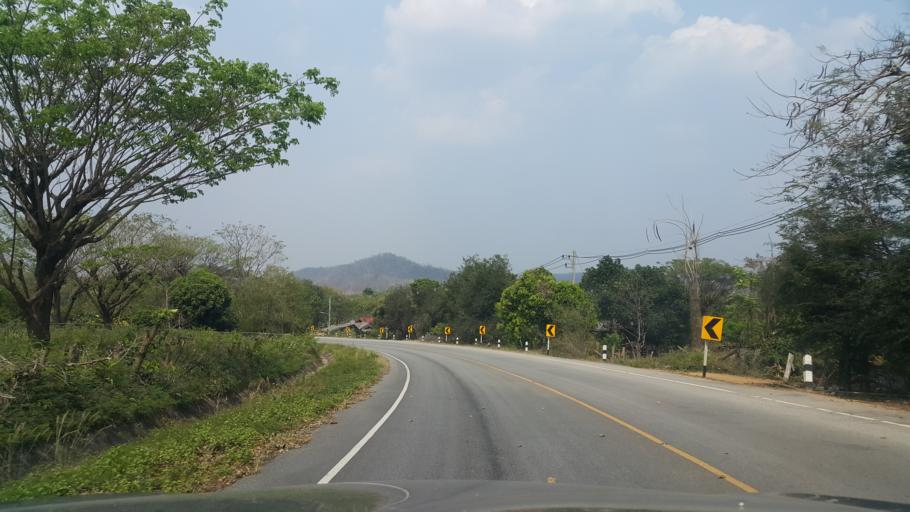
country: TH
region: Lamphun
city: Thung Hua Chang
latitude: 17.9167
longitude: 99.1500
